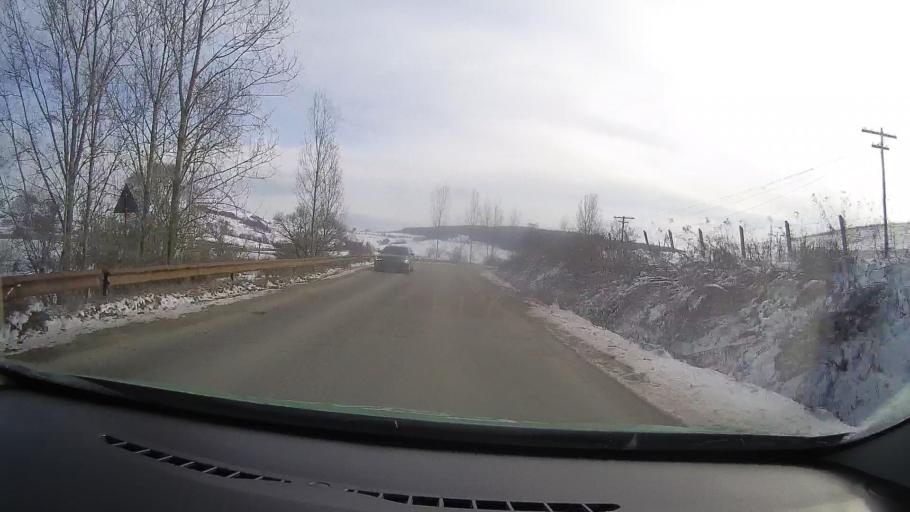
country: RO
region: Sibiu
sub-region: Oras Agnita
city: Ruja
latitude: 46.0006
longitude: 24.6727
